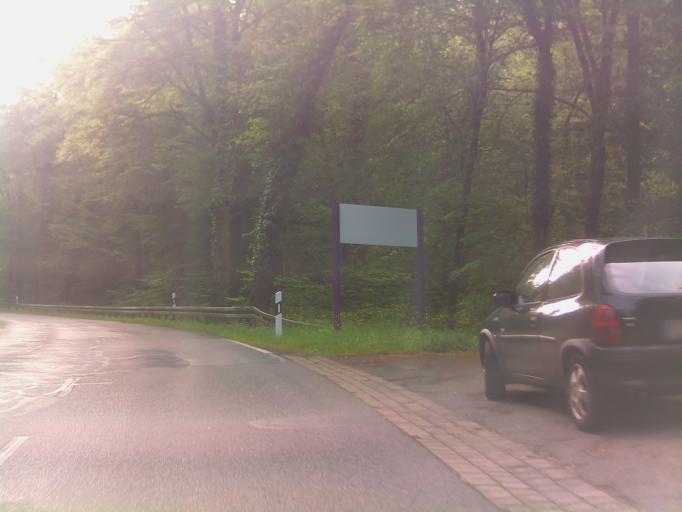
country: DE
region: Bavaria
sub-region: Regierungsbezirk Unterfranken
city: Klingenberg am Main
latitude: 49.7839
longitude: 9.1956
